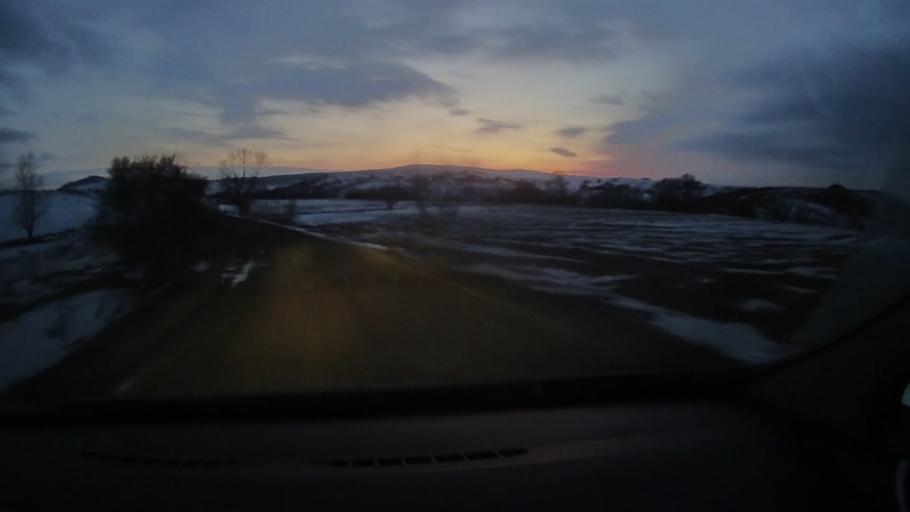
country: RO
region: Harghita
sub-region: Comuna Darjiu
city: Darjiu
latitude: 46.1611
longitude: 25.2077
